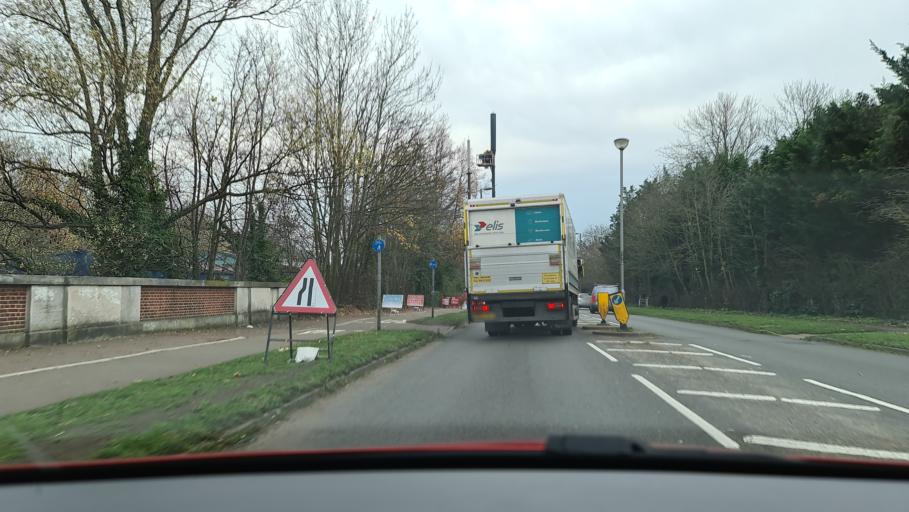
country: GB
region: England
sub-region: Surrey
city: East Molesey
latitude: 51.4011
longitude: -0.3430
